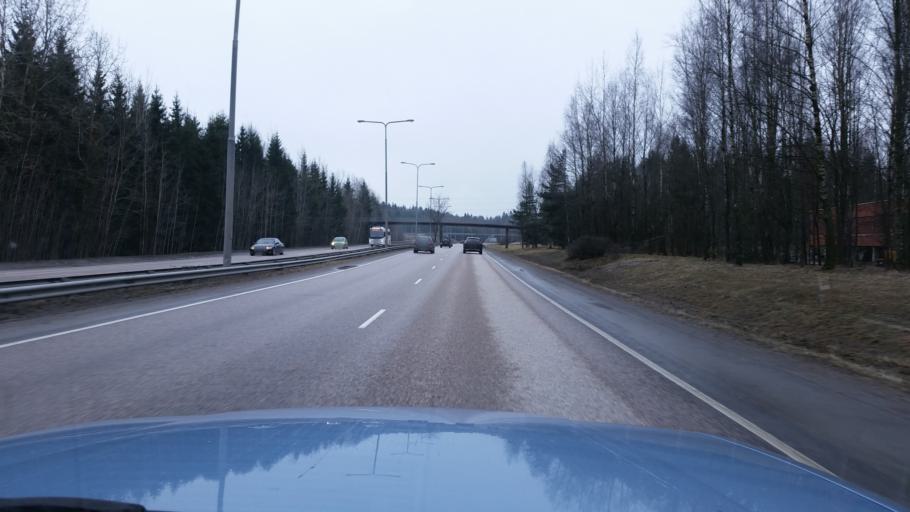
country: FI
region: Uusimaa
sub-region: Helsinki
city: Helsinki
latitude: 60.2254
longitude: 24.9077
